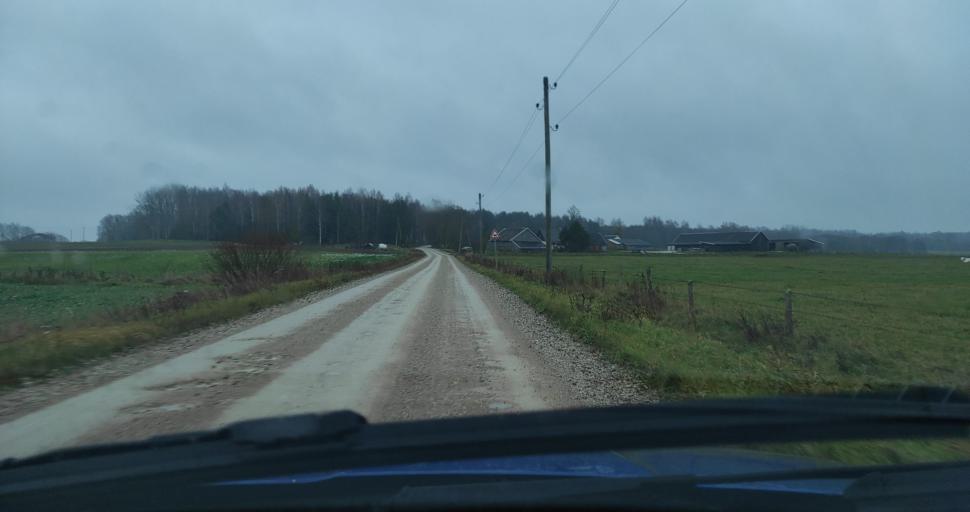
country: LV
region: Alsunga
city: Alsunga
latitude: 56.9018
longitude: 21.6286
